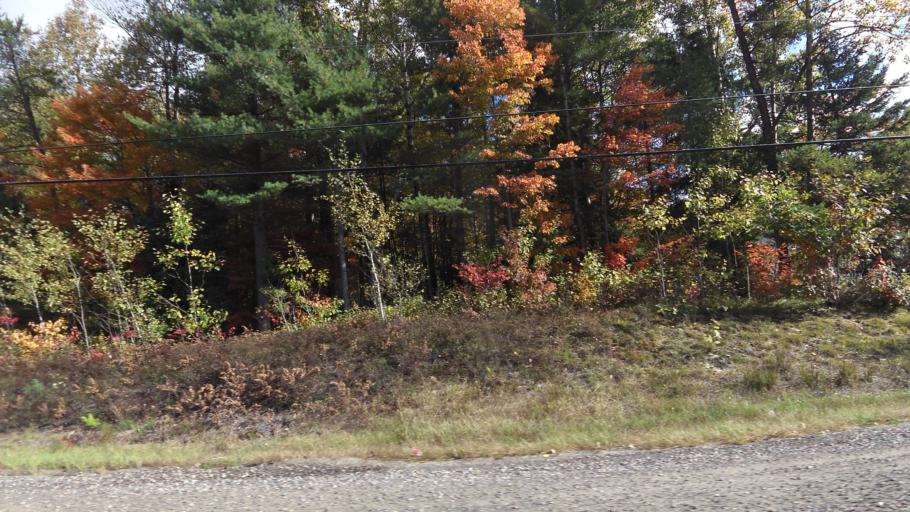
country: CA
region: Ontario
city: Deep River
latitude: 46.0832
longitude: -77.4849
